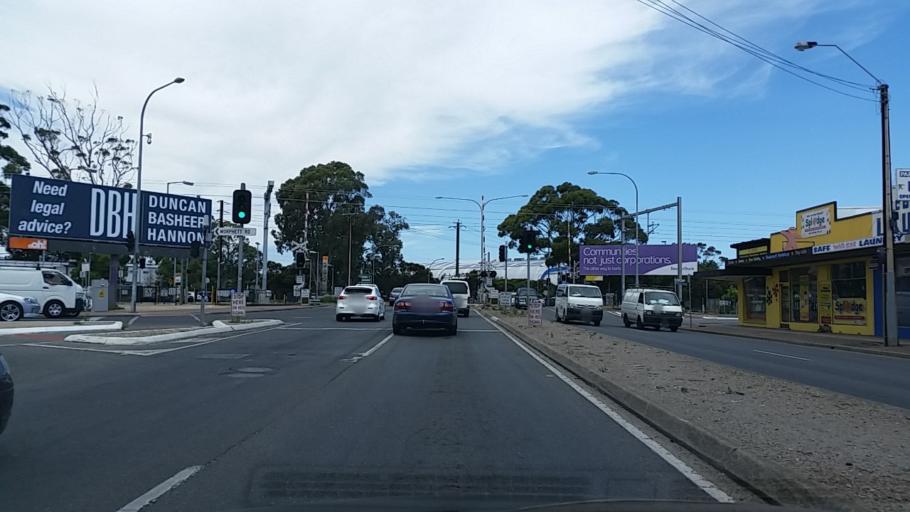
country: AU
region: South Australia
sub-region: Marion
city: Sturt
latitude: -35.0096
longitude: 138.5397
